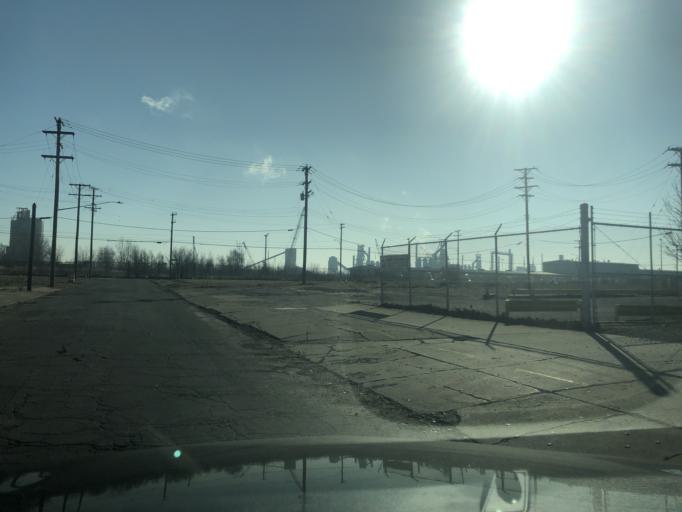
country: US
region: Michigan
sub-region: Wayne County
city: River Rouge
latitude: 42.2966
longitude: -83.1064
